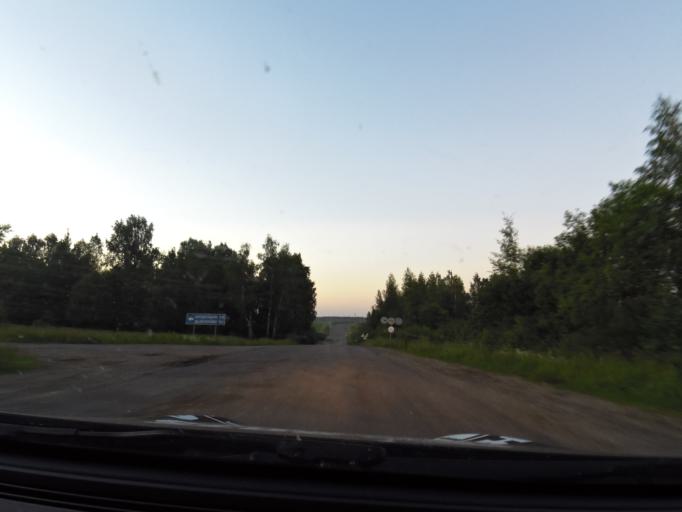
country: RU
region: Kostroma
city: Buy
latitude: 58.4780
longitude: 41.4387
